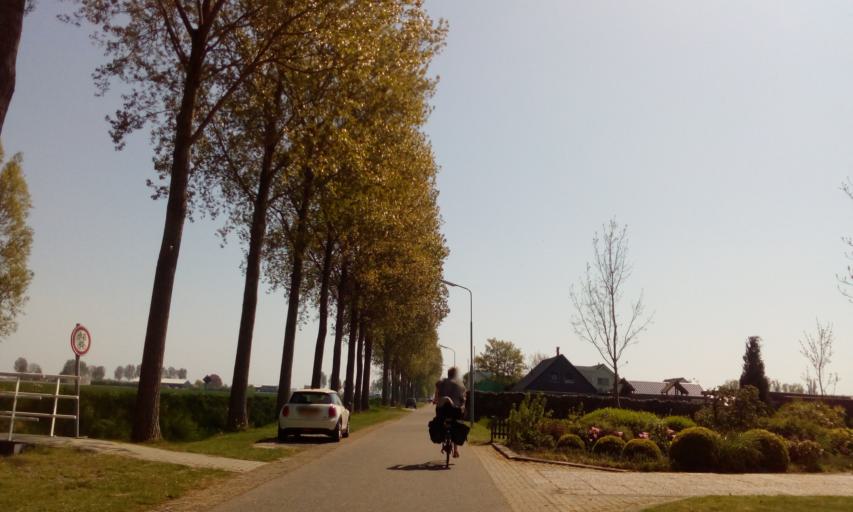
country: NL
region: South Holland
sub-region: Gemeente Kaag en Braassem
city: Leimuiden
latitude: 52.2567
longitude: 4.6488
